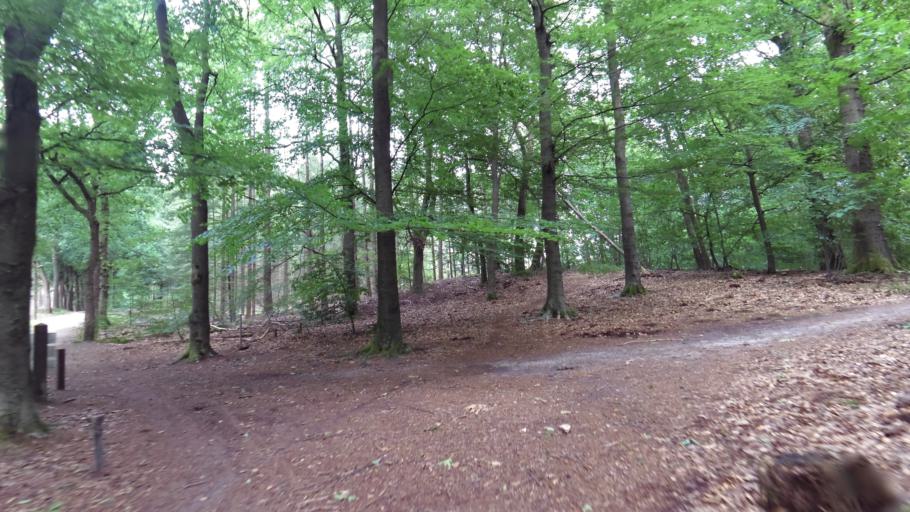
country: NL
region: Gelderland
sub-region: Gemeente Apeldoorn
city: Apeldoorn
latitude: 52.1910
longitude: 5.9129
